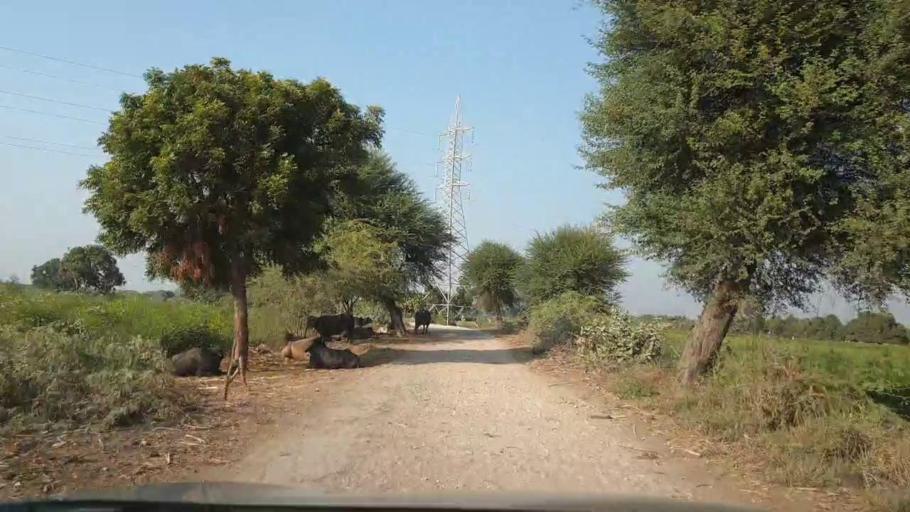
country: PK
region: Sindh
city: Tando Allahyar
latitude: 25.5069
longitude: 68.8520
